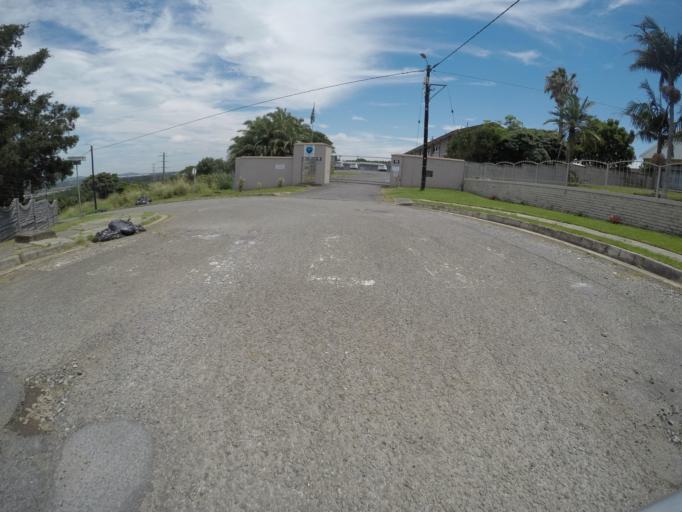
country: ZA
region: Eastern Cape
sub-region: Buffalo City Metropolitan Municipality
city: East London
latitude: -33.0380
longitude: 27.8494
